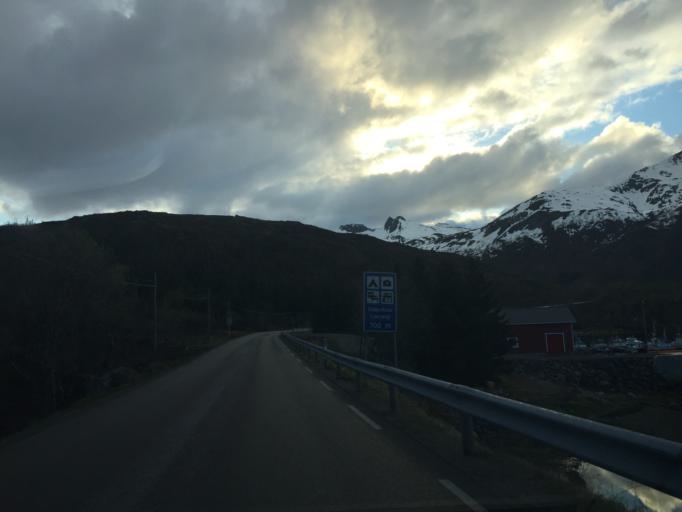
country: NO
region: Nordland
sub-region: Vagan
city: Svolvaer
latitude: 68.3187
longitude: 14.7050
